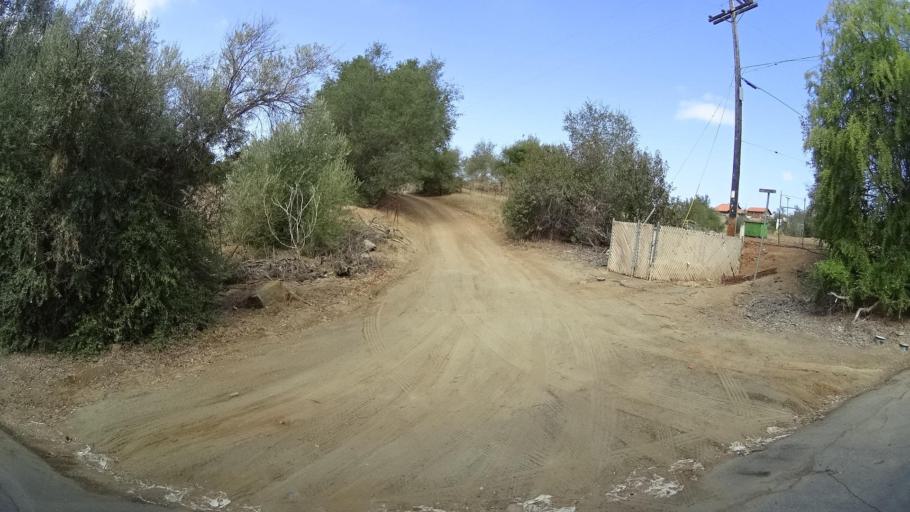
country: US
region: California
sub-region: San Diego County
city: Fallbrook
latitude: 33.4277
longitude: -117.2274
